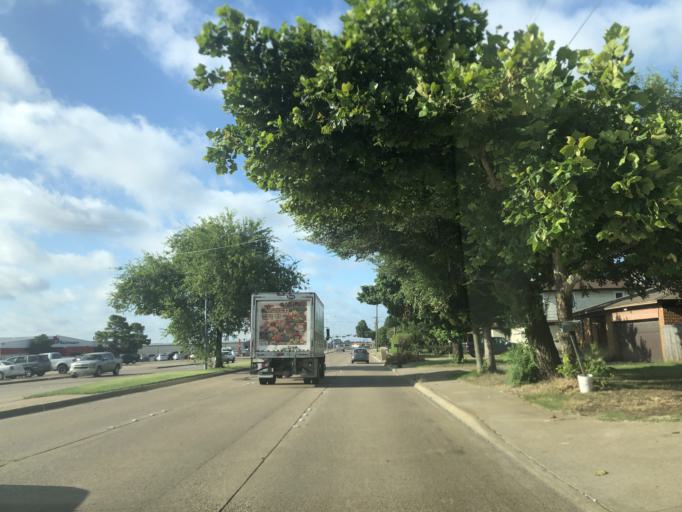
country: US
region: Texas
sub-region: Dallas County
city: Duncanville
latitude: 32.6689
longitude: -96.9088
